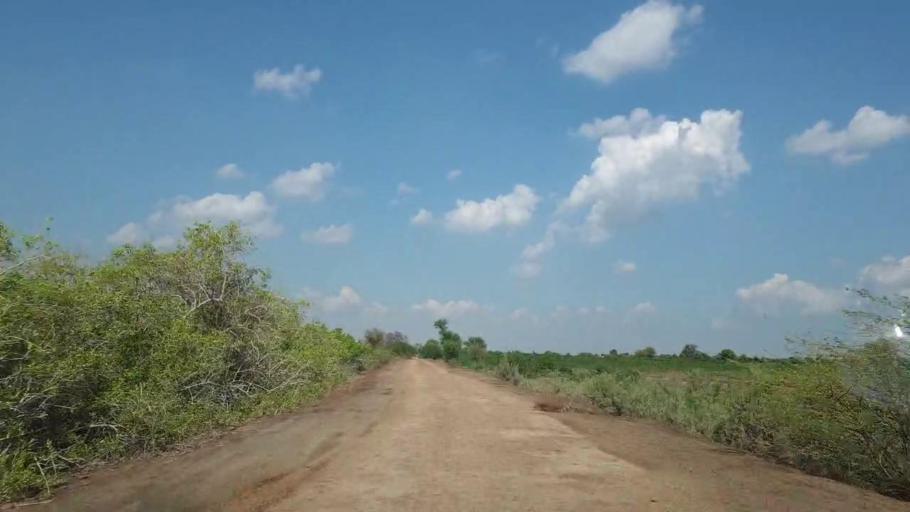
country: PK
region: Sindh
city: Pithoro
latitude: 25.6026
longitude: 69.3828
